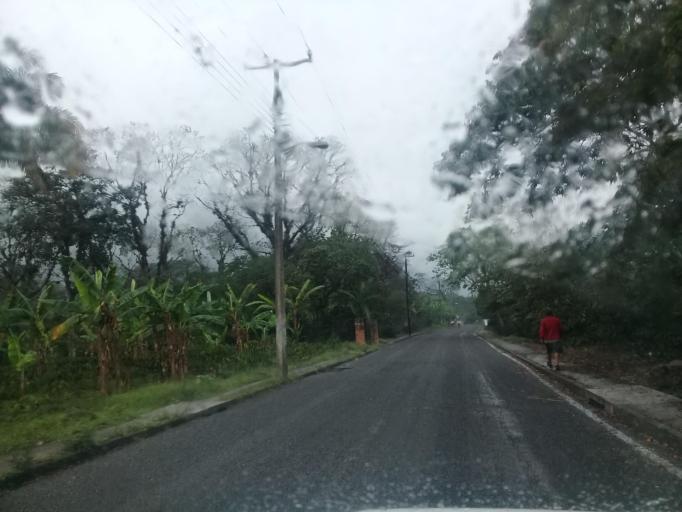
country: MX
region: Veracruz
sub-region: Amatlan de los Reyes
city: Centro de Readaptacion Social
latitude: 18.8010
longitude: -96.9466
